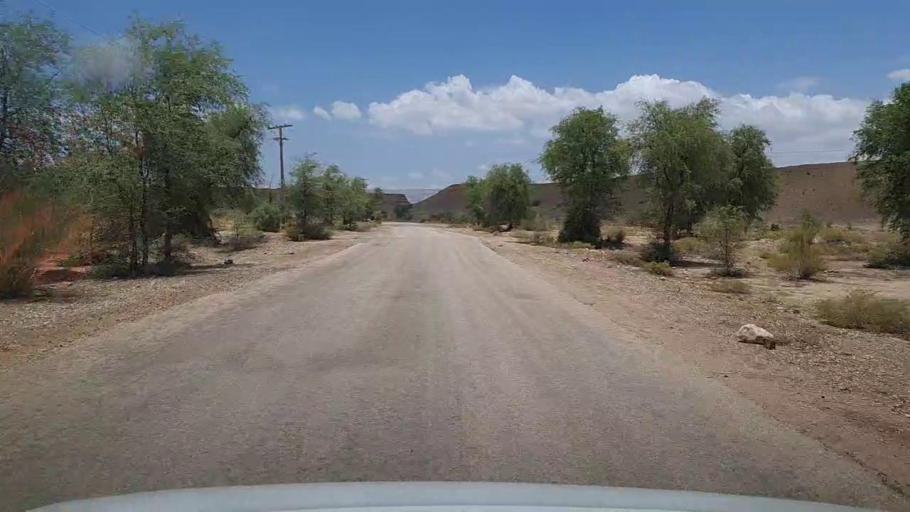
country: PK
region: Sindh
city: Bhan
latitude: 26.3167
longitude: 67.5922
